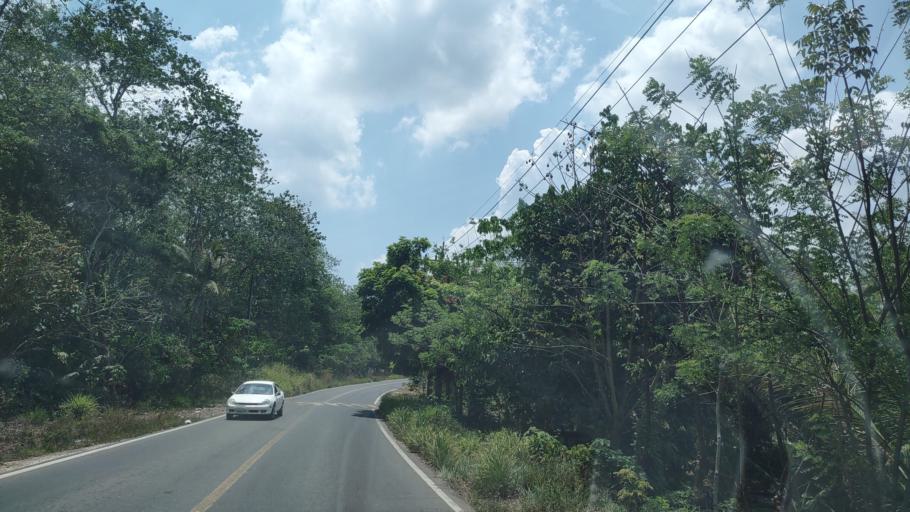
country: MX
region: Veracruz
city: Las Choapas
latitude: 17.9316
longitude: -94.1524
